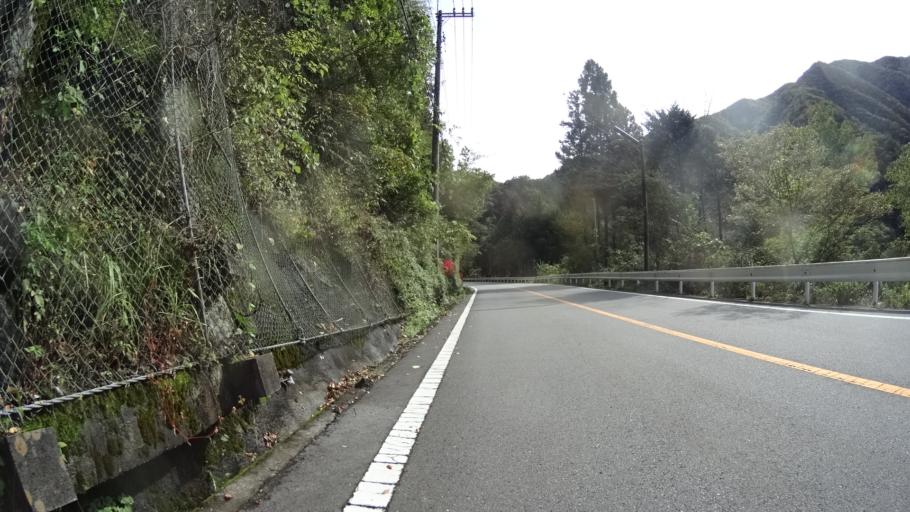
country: JP
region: Yamanashi
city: Otsuki
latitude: 35.7863
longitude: 138.9470
